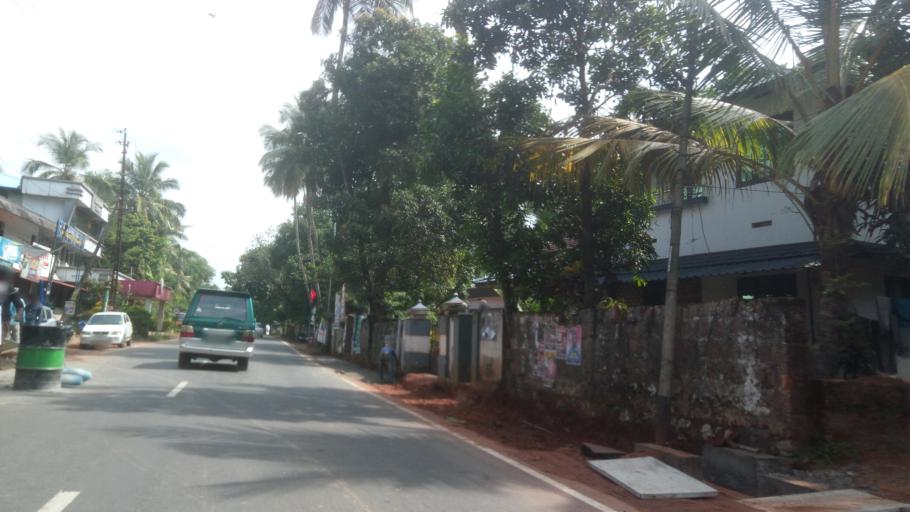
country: IN
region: Kerala
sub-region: Malappuram
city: Tirur
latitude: 10.8676
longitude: 76.0008
